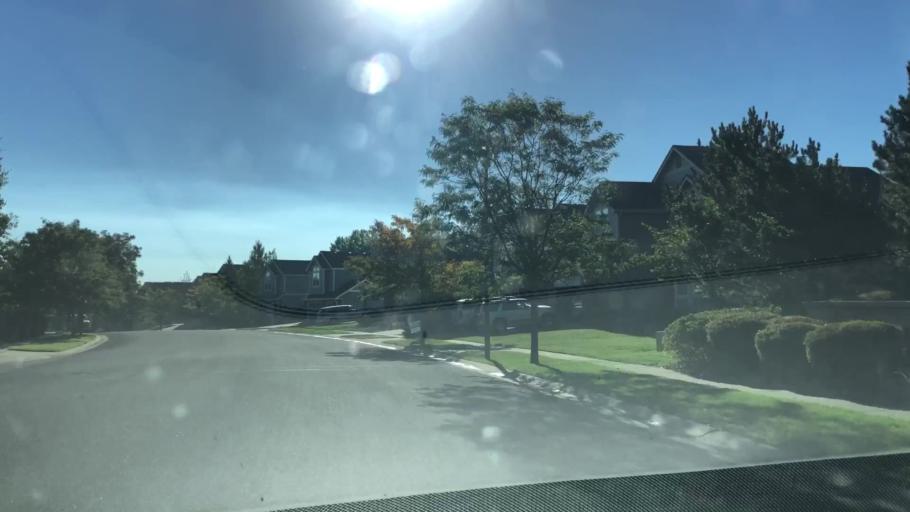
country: US
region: Colorado
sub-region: Larimer County
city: Loveland
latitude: 40.3960
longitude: -105.1386
